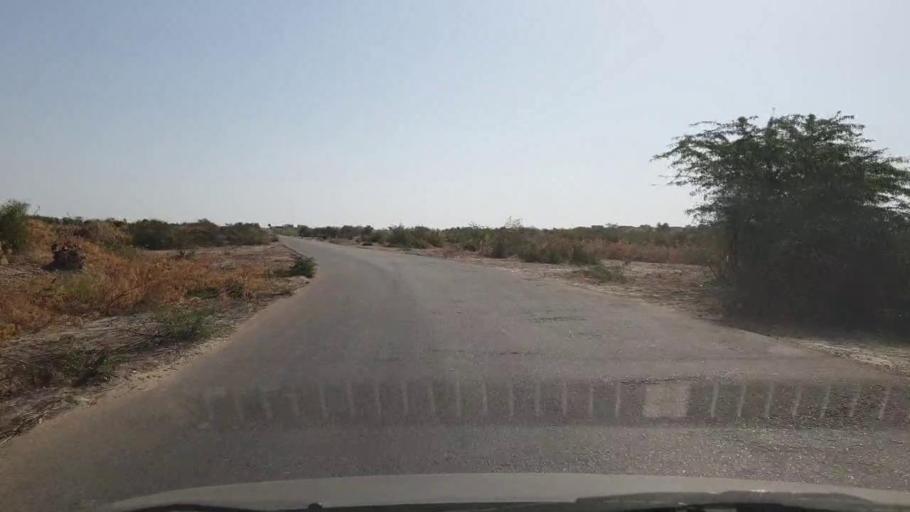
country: PK
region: Sindh
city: Chor
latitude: 25.4880
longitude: 69.7863
